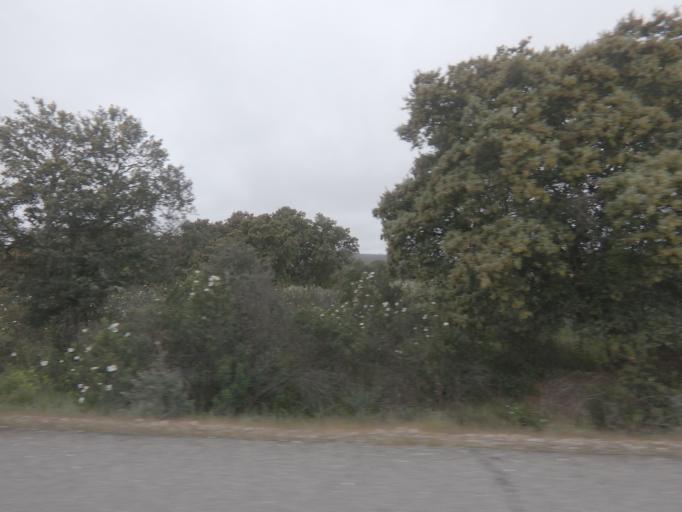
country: ES
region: Extremadura
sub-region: Provincia de Badajoz
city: Puebla de Obando
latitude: 39.2875
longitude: -6.5221
